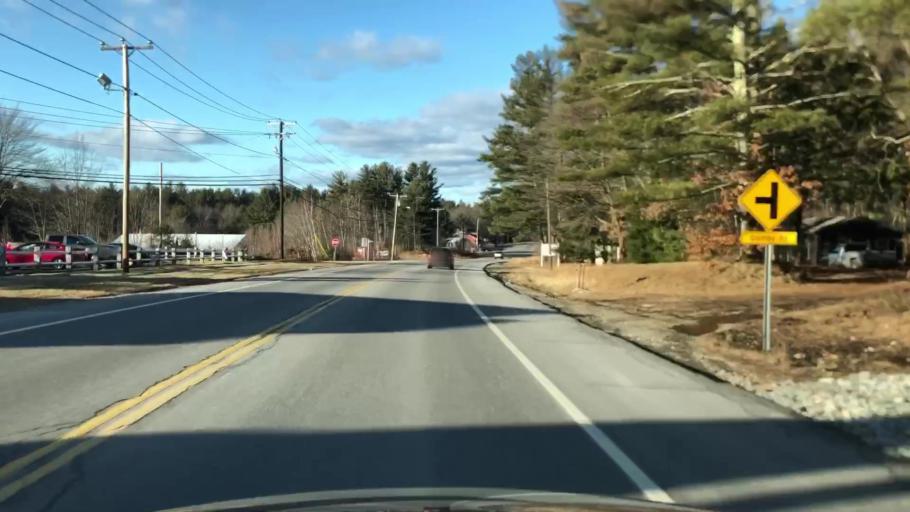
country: US
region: New Hampshire
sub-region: Hillsborough County
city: Brookline
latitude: 42.7535
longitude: -71.6726
